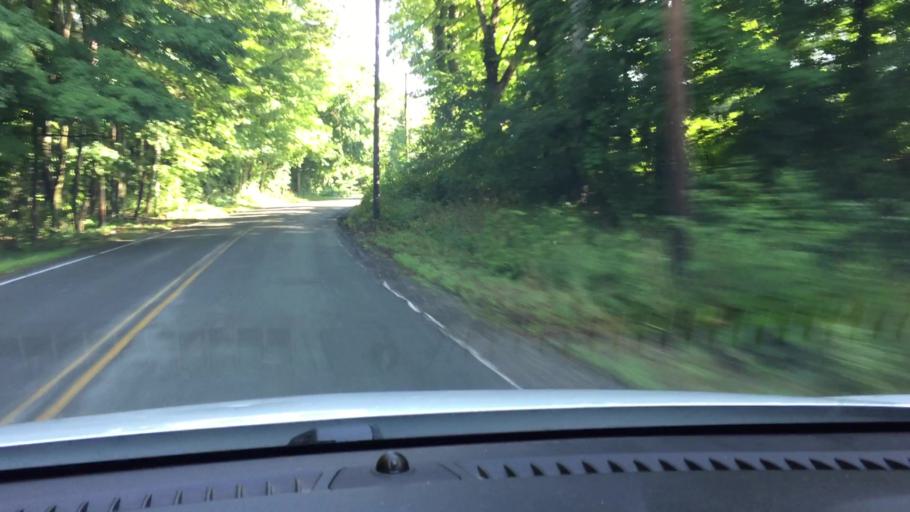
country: US
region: Massachusetts
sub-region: Berkshire County
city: Pittsfield
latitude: 42.4254
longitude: -73.2255
